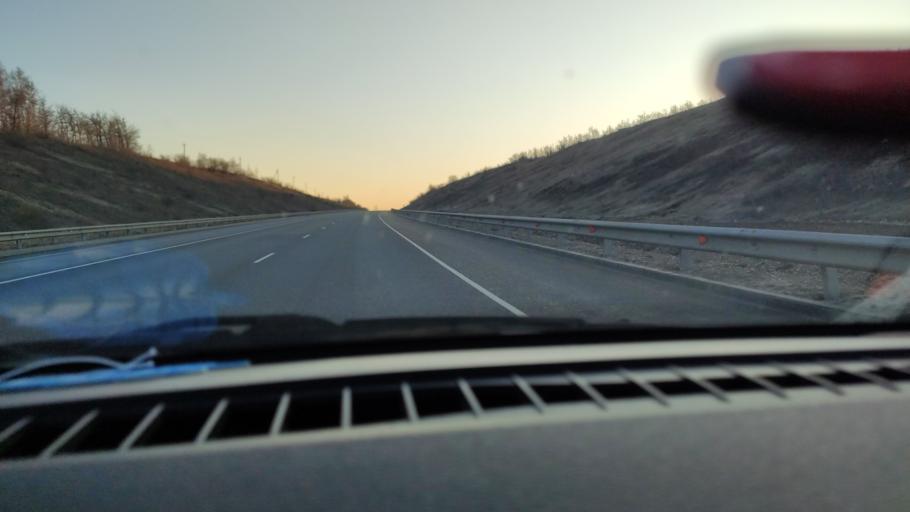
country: RU
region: Saratov
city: Yelshanka
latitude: 51.8851
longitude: 46.5154
